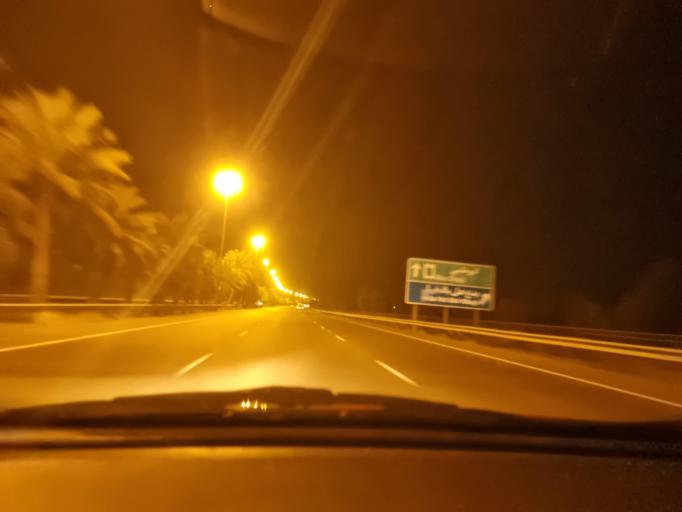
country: AE
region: Abu Dhabi
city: Al Ain
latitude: 24.1717
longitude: 55.2853
